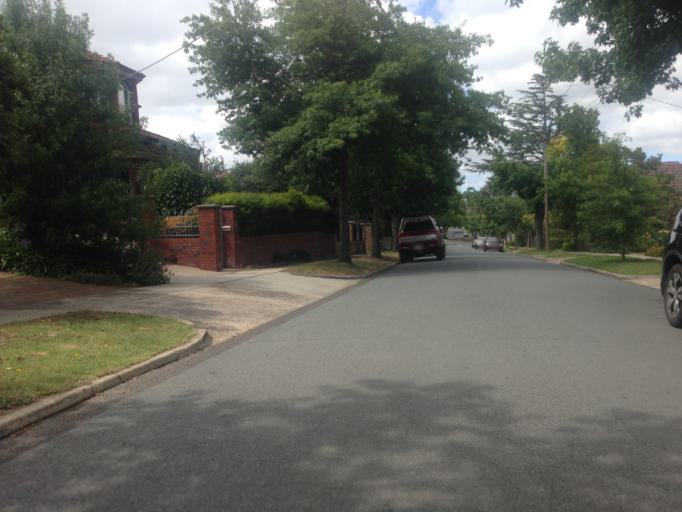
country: AU
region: Victoria
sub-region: Boroondara
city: Balwyn North
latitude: -37.7893
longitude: 145.0800
